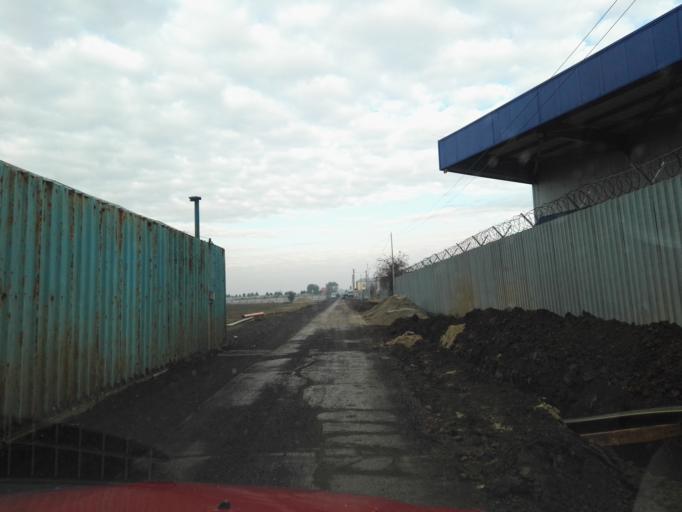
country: RO
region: Ilfov
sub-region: Comuna Magurele
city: Magurele
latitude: 44.3755
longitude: 26.0449
